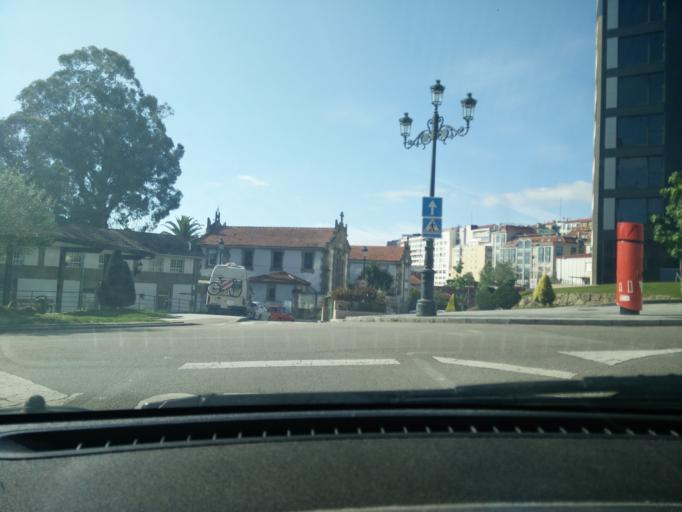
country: ES
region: Galicia
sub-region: Provincia de Pontevedra
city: Vigo
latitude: 42.2246
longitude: -8.7272
